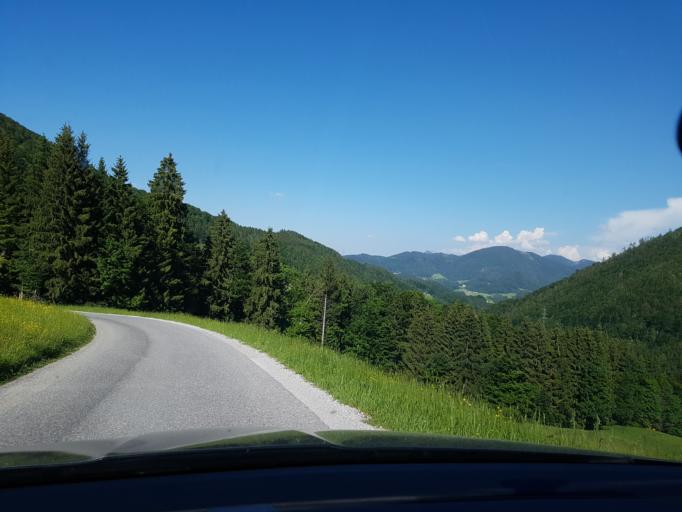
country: AT
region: Salzburg
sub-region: Politischer Bezirk Salzburg-Umgebung
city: Koppl
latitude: 47.7947
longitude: 13.1214
